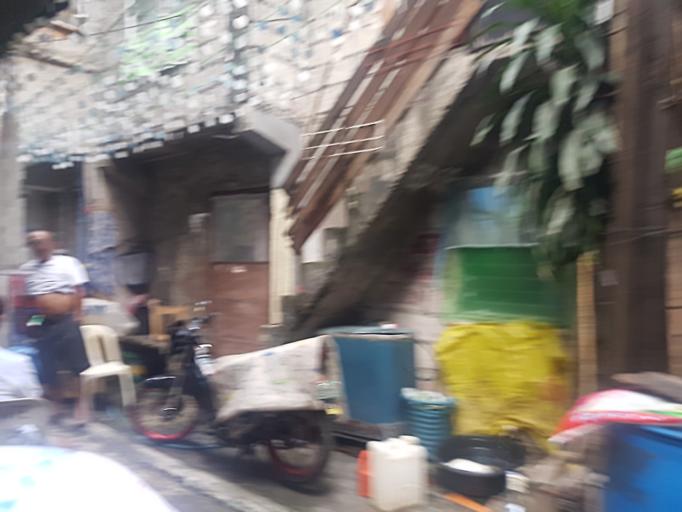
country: PH
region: Metro Manila
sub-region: City of Manila
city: Quiapo
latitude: 14.5875
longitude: 121.0004
